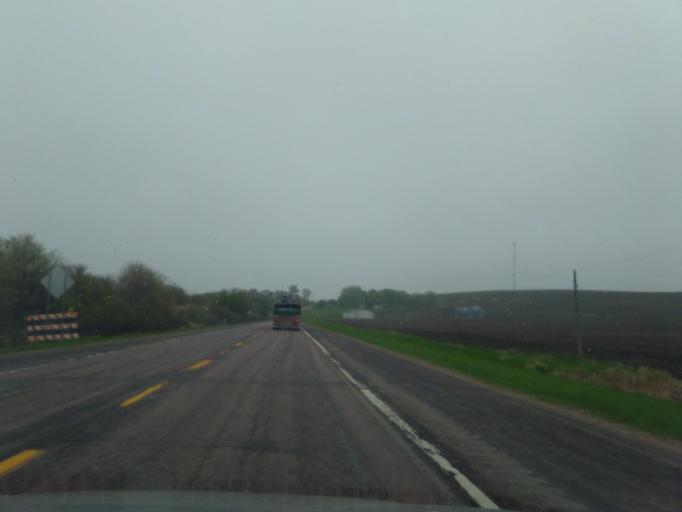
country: US
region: Nebraska
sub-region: Burt County
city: Oakland
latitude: 41.8154
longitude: -96.4732
